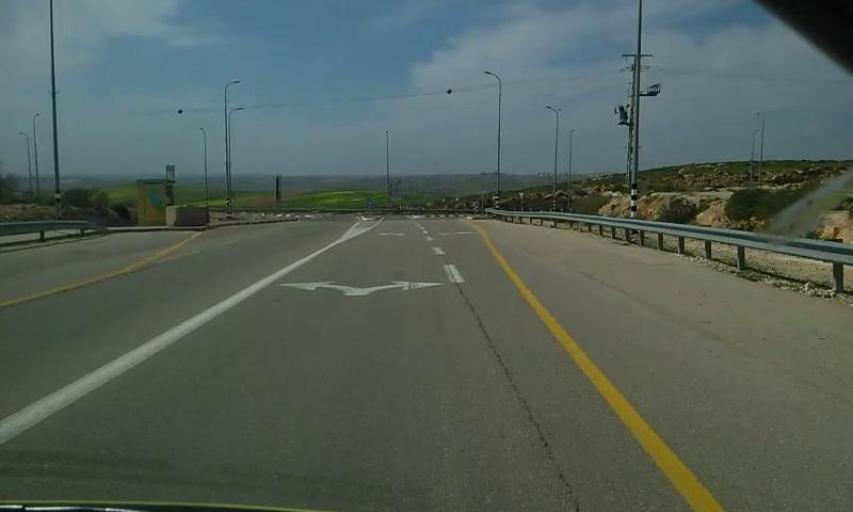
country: PS
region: West Bank
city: Az Zahiriyah
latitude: 31.3770
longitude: 35.0043
